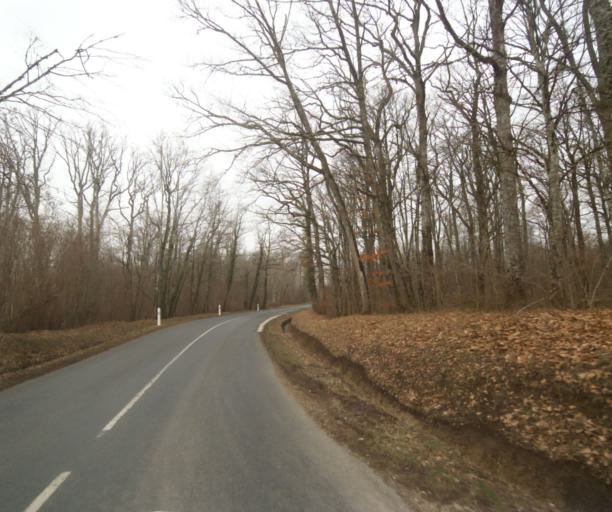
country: FR
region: Champagne-Ardenne
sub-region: Departement de la Marne
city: Pargny-sur-Saulx
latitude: 48.7305
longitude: 4.8657
